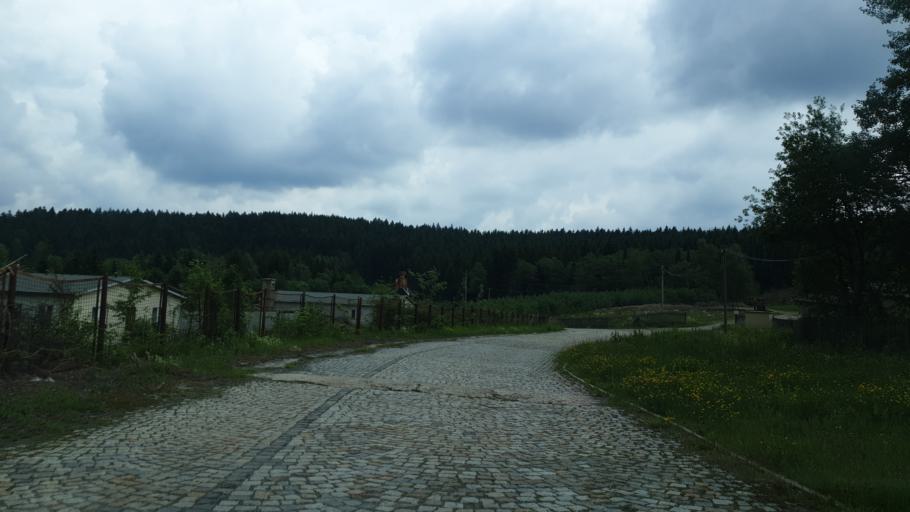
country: DE
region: Saxony
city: Tannenbergsthal
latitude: 50.4175
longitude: 12.4540
